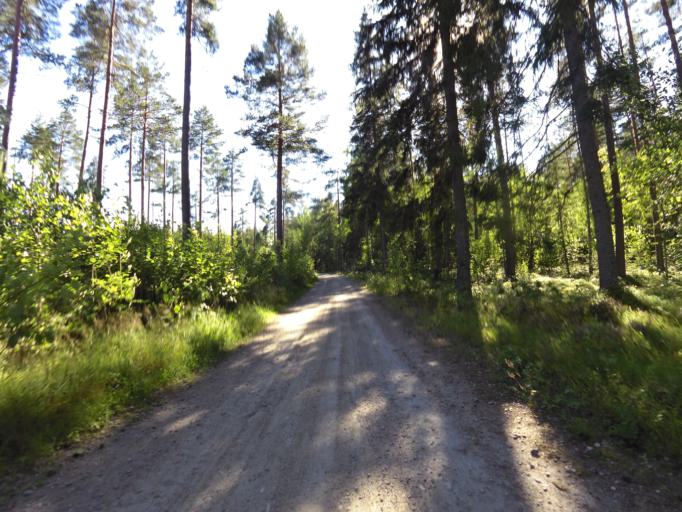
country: SE
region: Gaevleborg
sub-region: Hofors Kommun
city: Hofors
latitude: 60.5744
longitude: 16.4271
